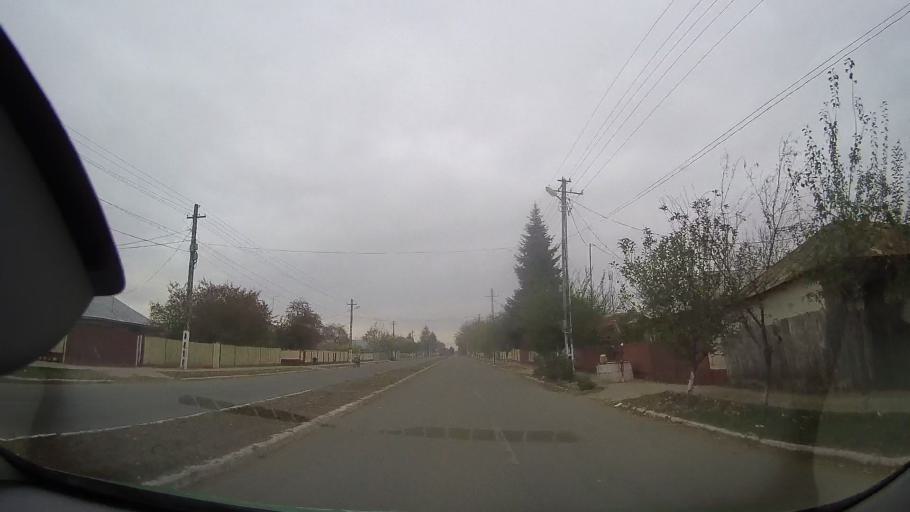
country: RO
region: Buzau
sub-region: Comuna Rusetu
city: Rusetu
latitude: 44.9593
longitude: 27.2156
